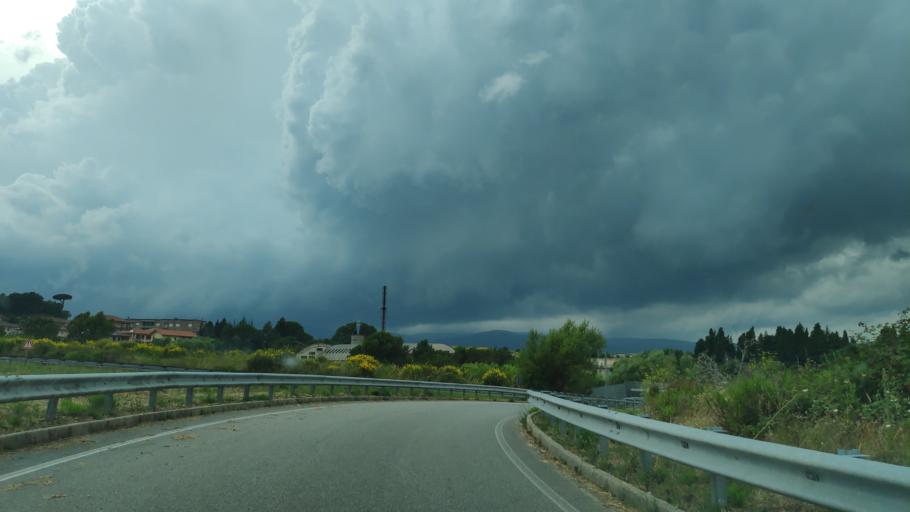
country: IT
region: Calabria
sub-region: Provincia di Catanzaro
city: Argusto
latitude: 38.6801
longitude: 16.4251
